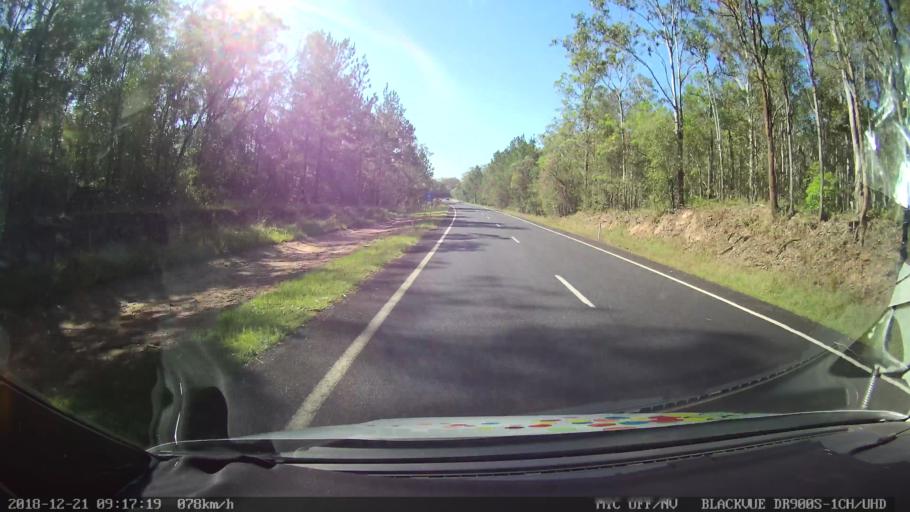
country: AU
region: New South Wales
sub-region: Clarence Valley
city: Maclean
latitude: -29.2909
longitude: 152.9900
